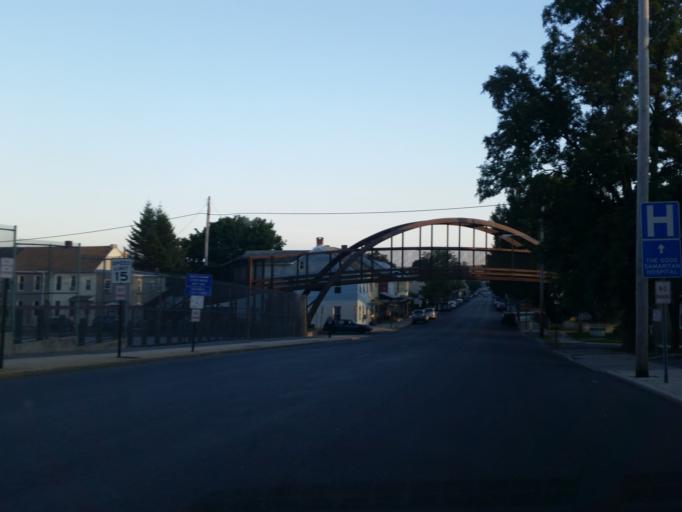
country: US
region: Pennsylvania
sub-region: Lebanon County
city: Sand Hill
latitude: 40.3493
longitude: -76.4293
